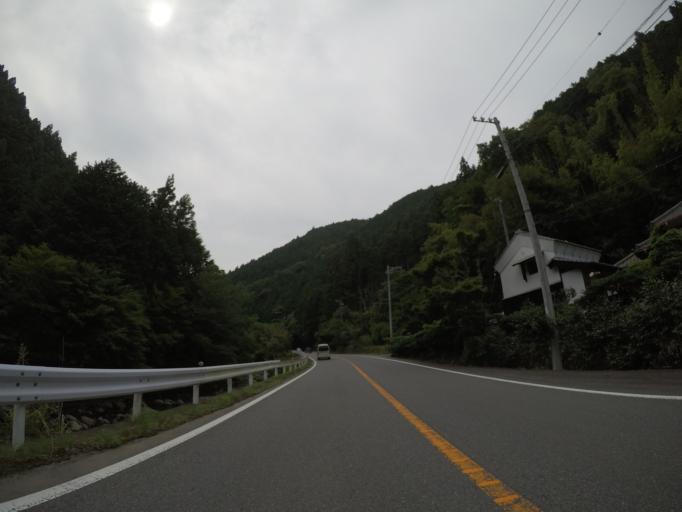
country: JP
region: Shizuoka
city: Fujinomiya
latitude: 35.1960
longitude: 138.5361
